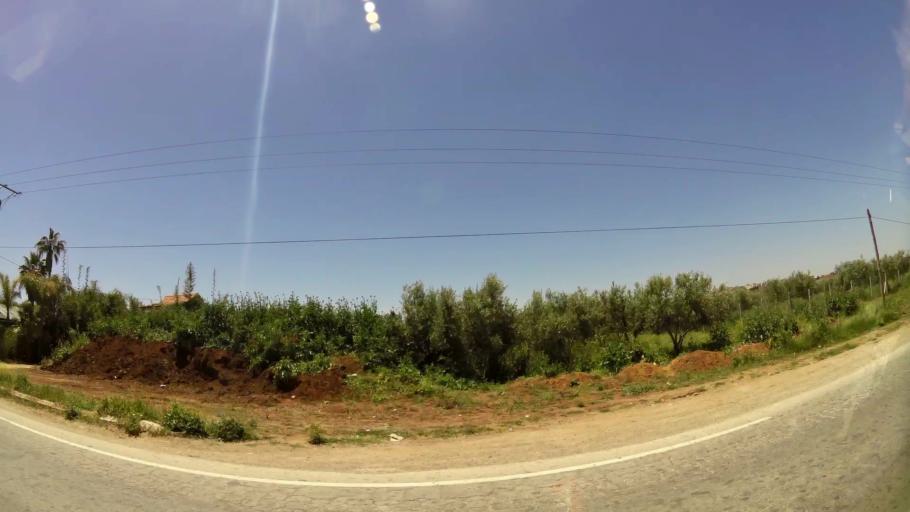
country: MA
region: Meknes-Tafilalet
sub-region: Meknes
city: Meknes
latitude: 33.8553
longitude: -5.5725
